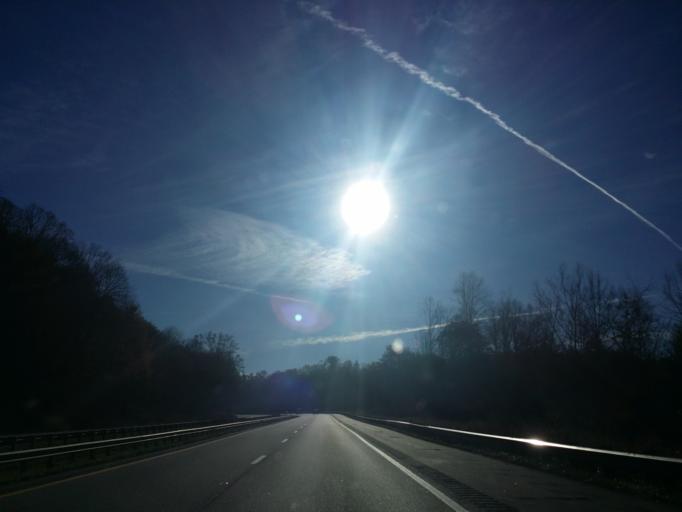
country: US
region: North Carolina
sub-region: McDowell County
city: West Marion
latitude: 35.6388
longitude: -82.1107
